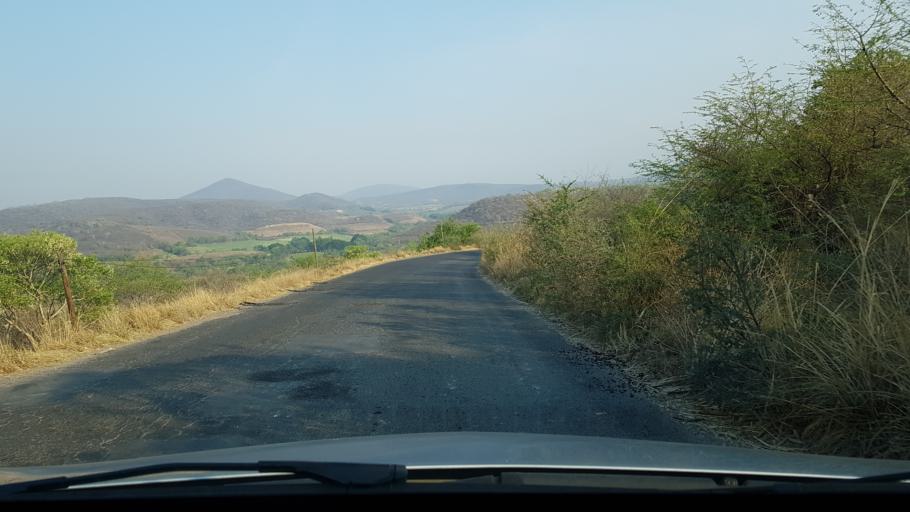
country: MX
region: Morelos
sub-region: Tepalcingo
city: Zacapalco
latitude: 18.6305
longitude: -99.0096
